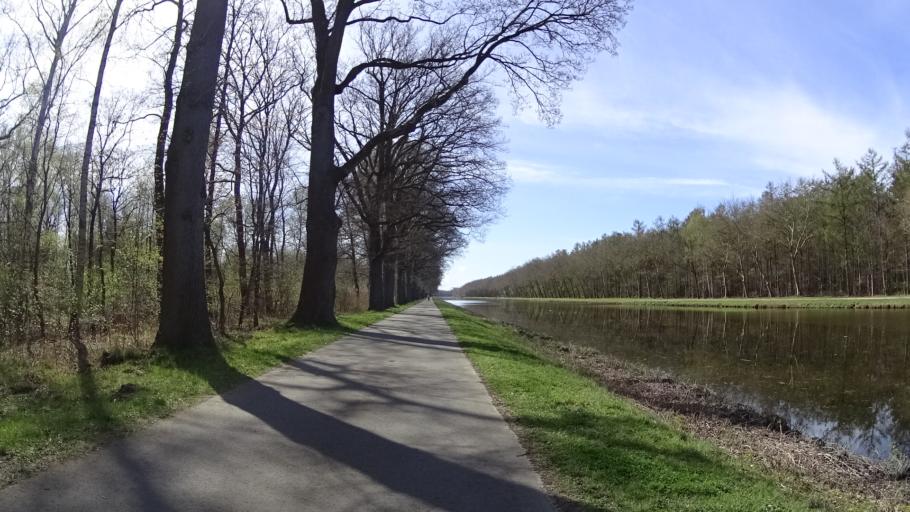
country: DE
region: Lower Saxony
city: Geeste
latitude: 52.5907
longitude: 7.3106
